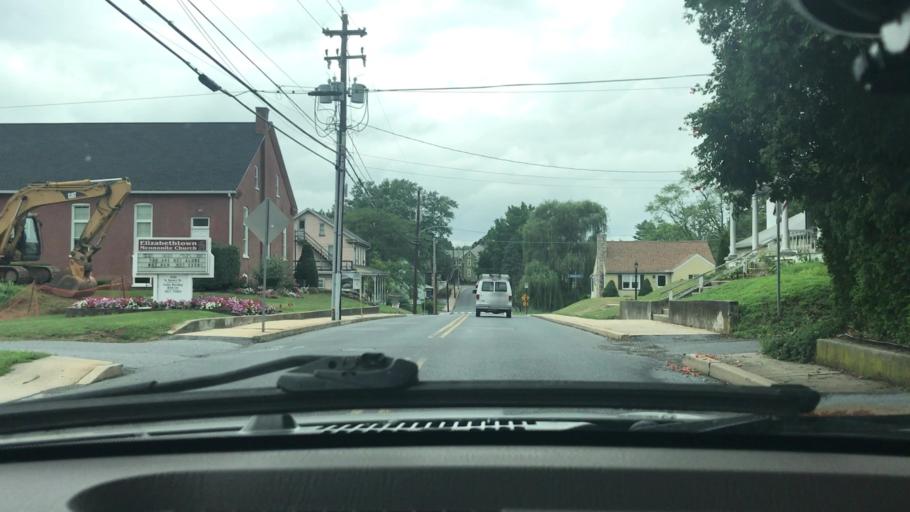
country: US
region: Pennsylvania
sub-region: Lancaster County
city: Elizabethtown
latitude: 40.1489
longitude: -76.5998
